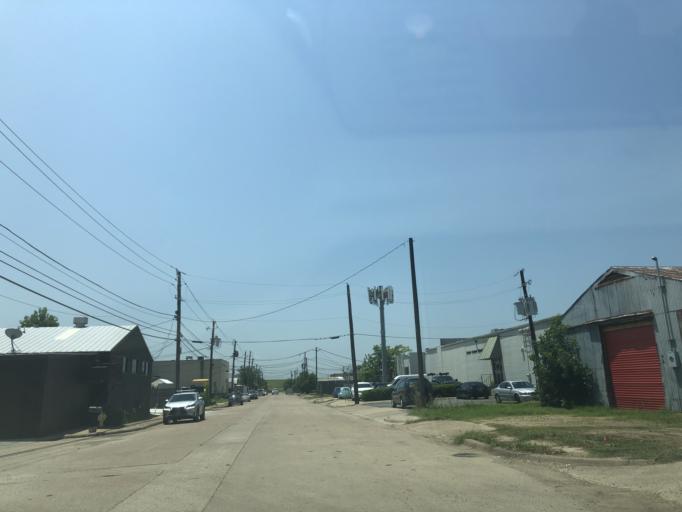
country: US
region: Texas
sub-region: Dallas County
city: Dallas
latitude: 32.8056
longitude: -96.8512
